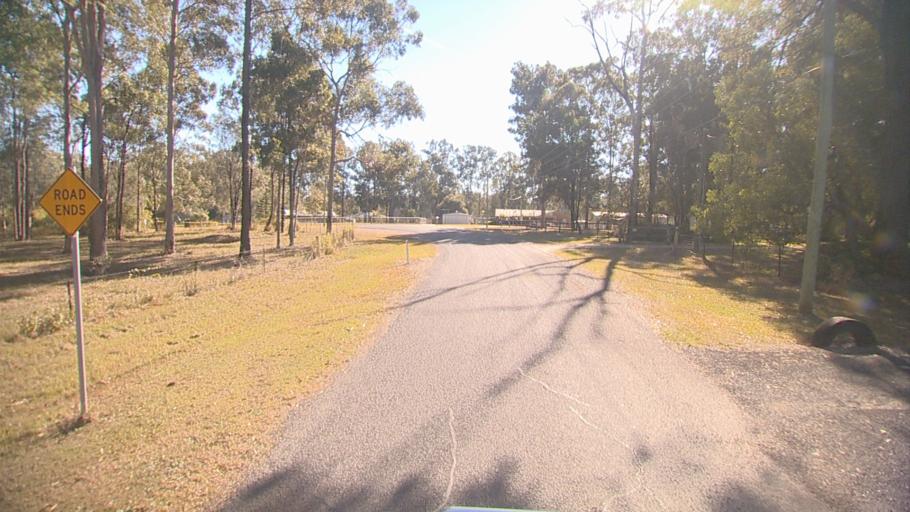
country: AU
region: Queensland
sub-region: Logan
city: Chambers Flat
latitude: -27.7928
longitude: 153.1418
